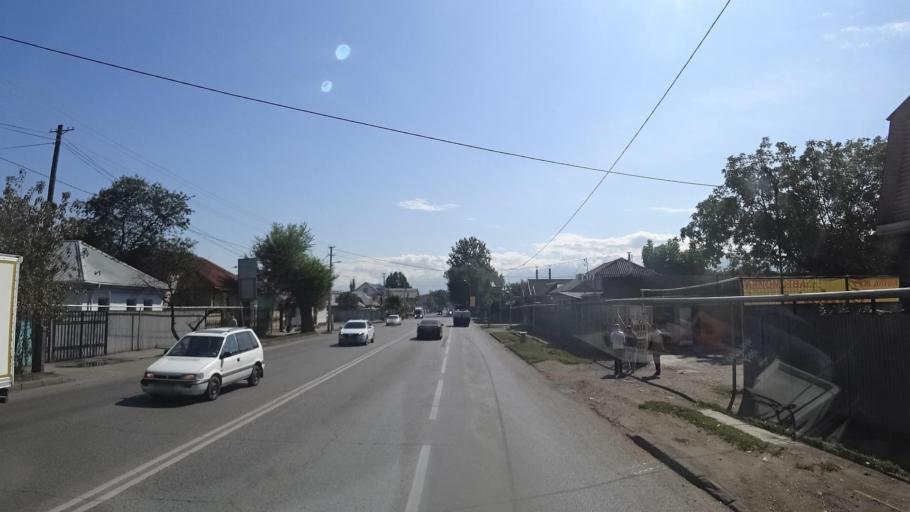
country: KZ
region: Almaty Oblysy
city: Pervomayskiy
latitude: 43.3532
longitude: 76.9535
